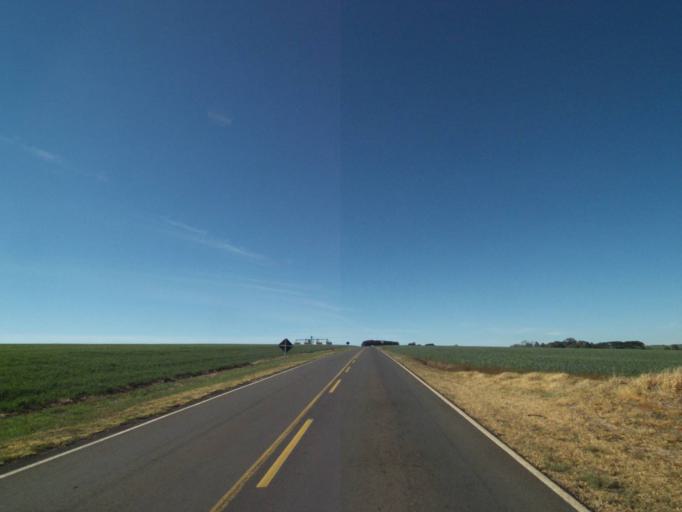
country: BR
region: Parana
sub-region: Tibagi
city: Tibagi
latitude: -24.5373
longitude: -50.3124
